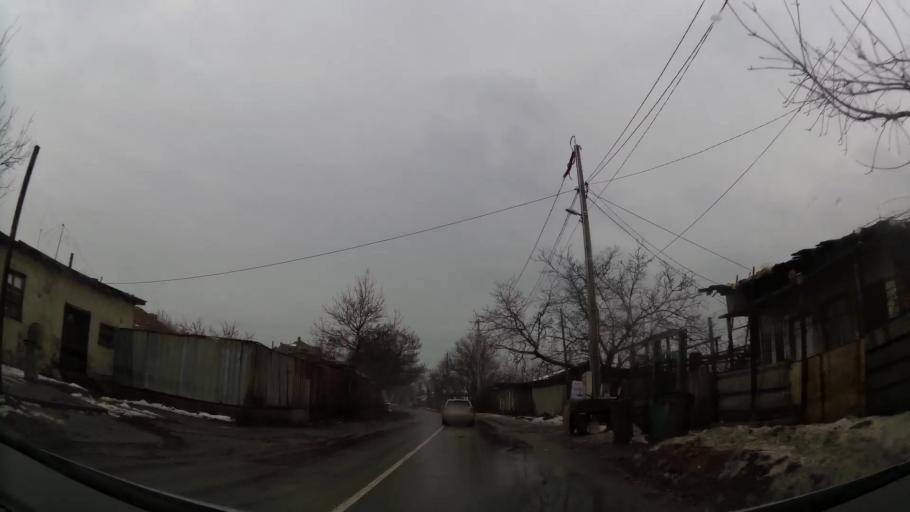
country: BG
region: Sofia-Capital
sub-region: Stolichna Obshtina
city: Sofia
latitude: 42.6952
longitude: 23.2575
